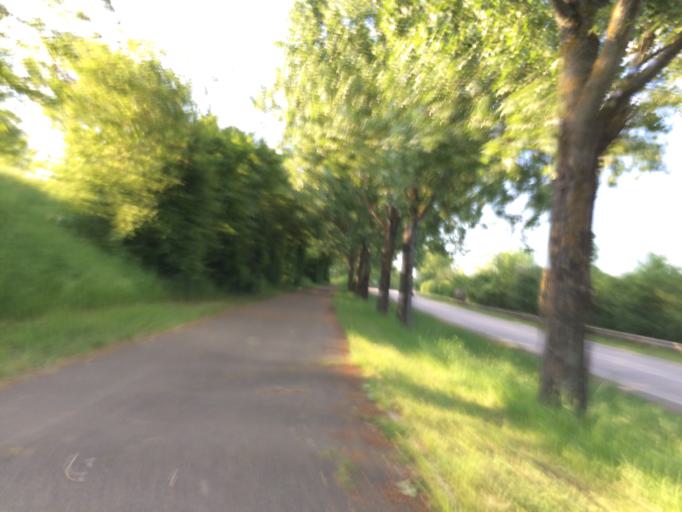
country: FR
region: Ile-de-France
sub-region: Departement de l'Essonne
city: Lisses
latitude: 48.6089
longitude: 2.4245
